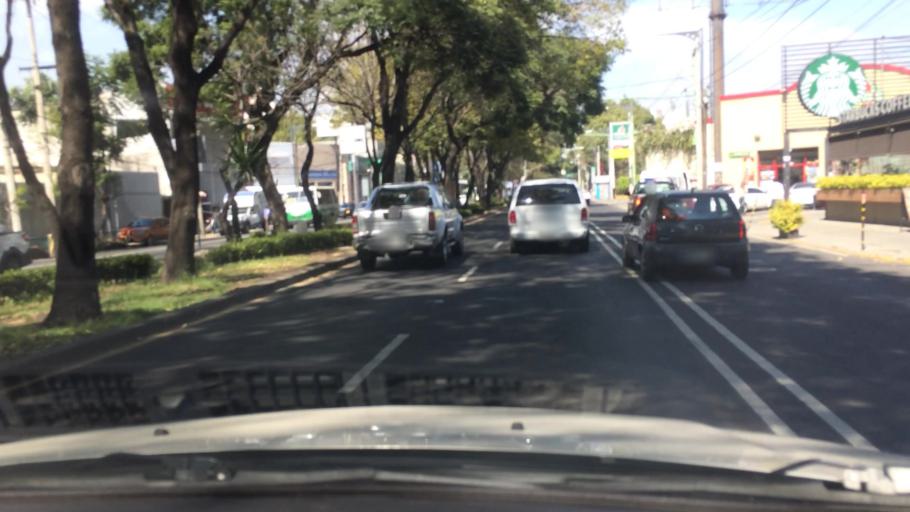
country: MX
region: Mexico City
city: Coyoacan
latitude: 19.3538
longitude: -99.1520
